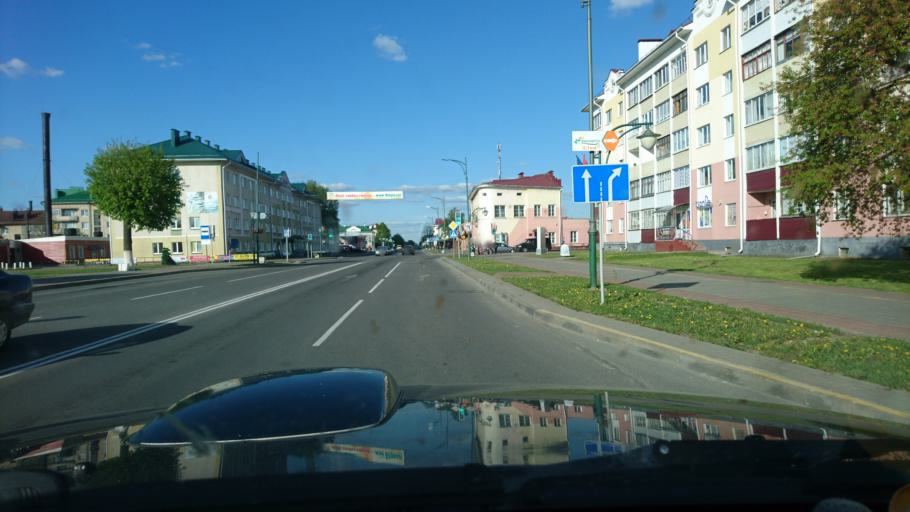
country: BY
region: Brest
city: Byaroza
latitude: 52.5331
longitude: 24.9823
